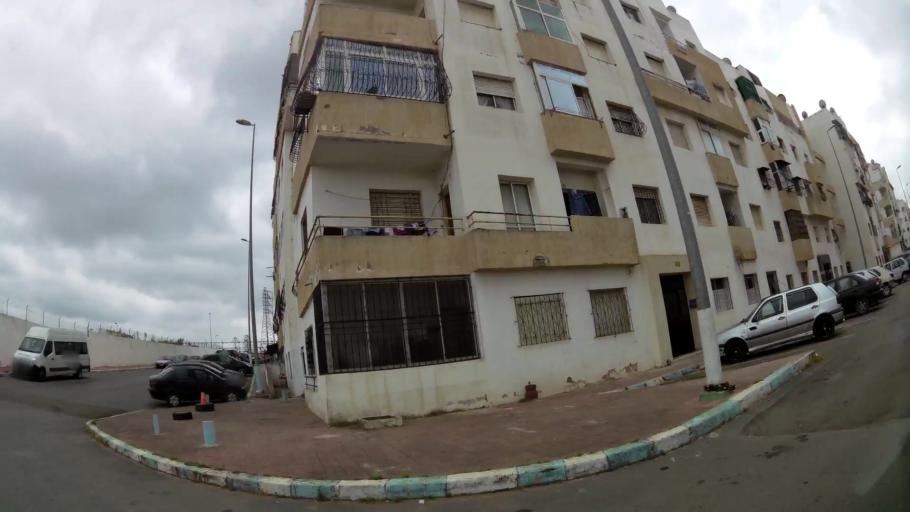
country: MA
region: Rabat-Sale-Zemmour-Zaer
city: Sale
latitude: 34.0417
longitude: -6.7974
